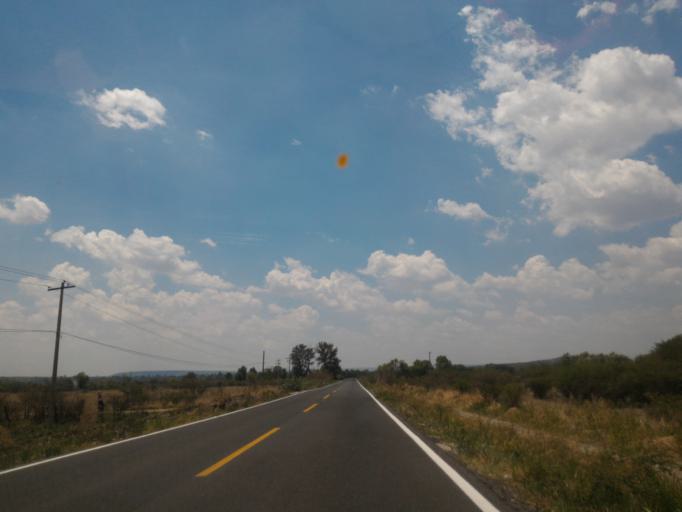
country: MX
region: Guanajuato
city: Ciudad Manuel Doblado
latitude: 20.7823
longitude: -101.9795
